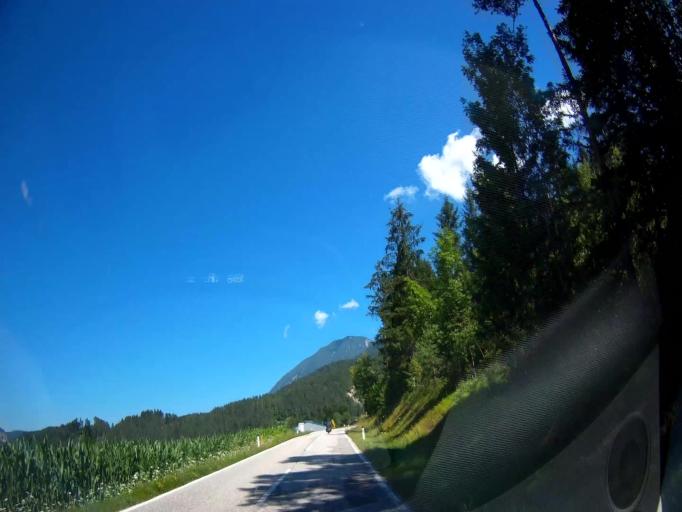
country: AT
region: Carinthia
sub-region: Politischer Bezirk Klagenfurt Land
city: Ebenthal
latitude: 46.5380
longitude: 14.3926
